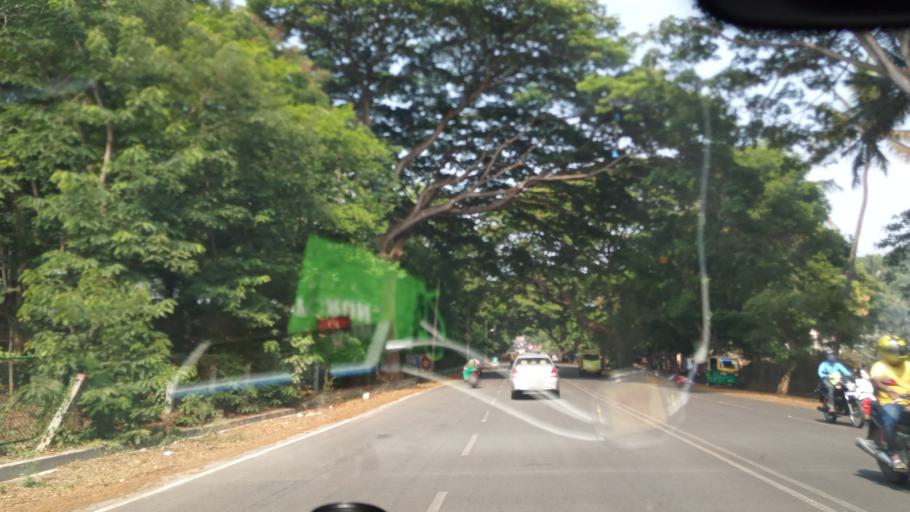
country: IN
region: Karnataka
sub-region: Mysore
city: Mysore
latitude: 12.3064
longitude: 76.6289
